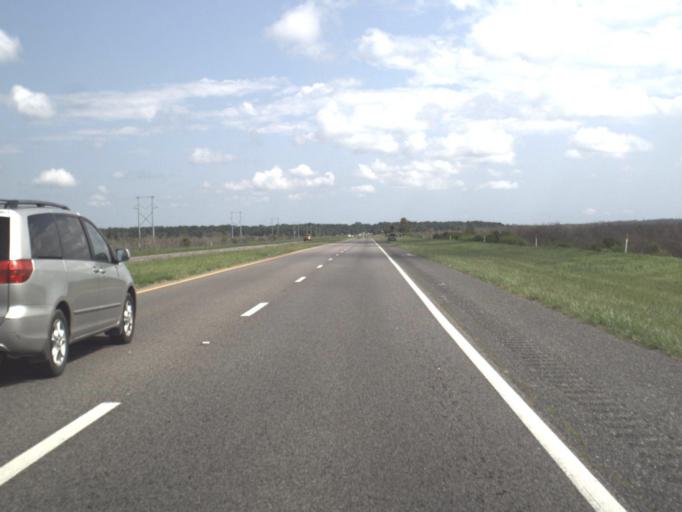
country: US
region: Florida
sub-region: Alachua County
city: Gainesville
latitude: 29.5687
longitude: -82.3338
